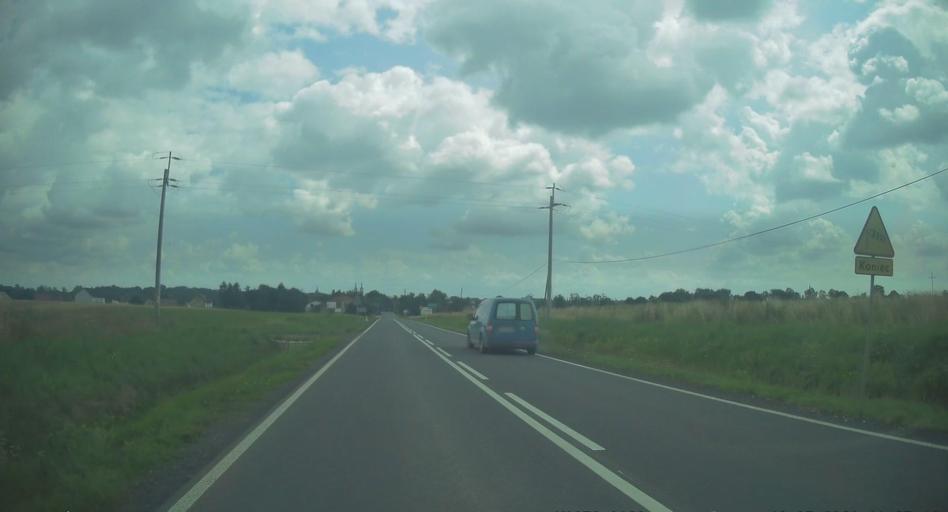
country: PL
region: Opole Voivodeship
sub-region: Powiat prudnicki
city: Glogowek
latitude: 50.3529
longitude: 17.8393
